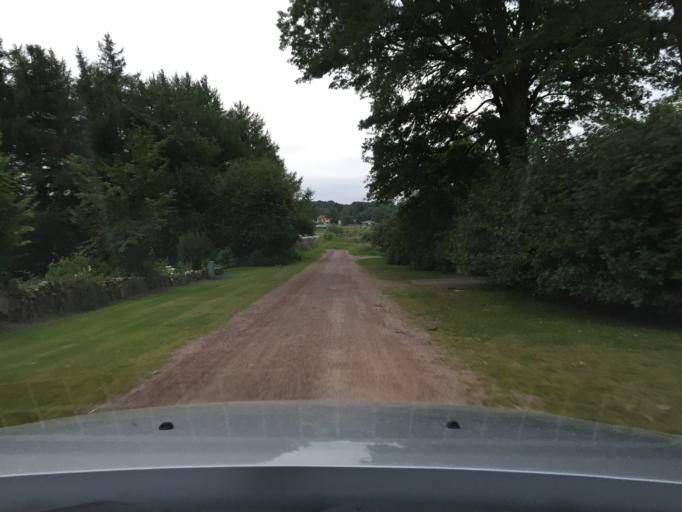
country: SE
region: Skane
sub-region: Hassleholms Kommun
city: Sosdala
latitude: 56.0553
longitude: 13.7242
